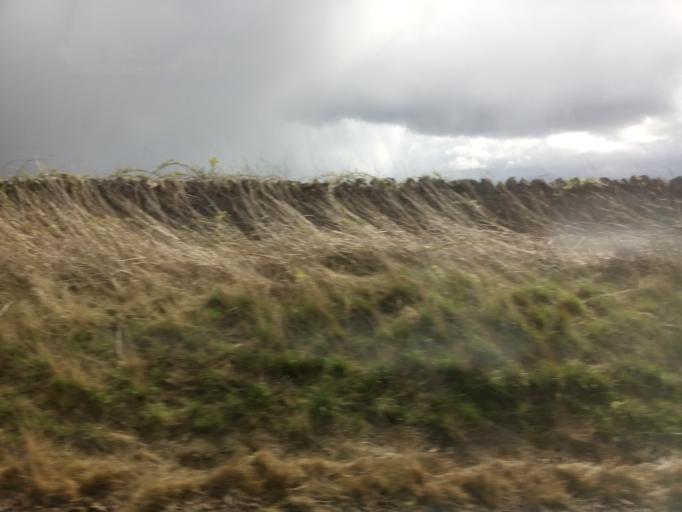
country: GB
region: Scotland
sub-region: East Lothian
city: Gullane
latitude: 56.0036
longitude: -2.7958
